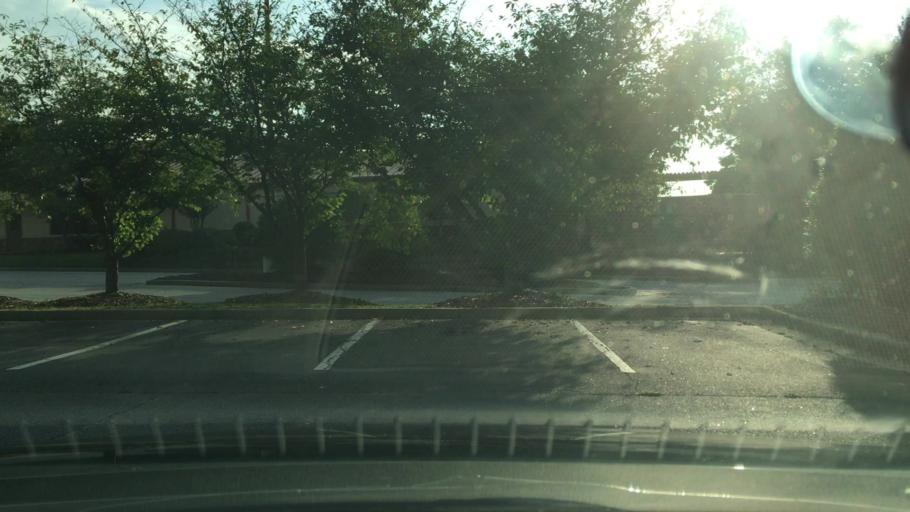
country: US
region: Georgia
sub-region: Coweta County
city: Newnan
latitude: 33.3954
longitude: -84.7586
